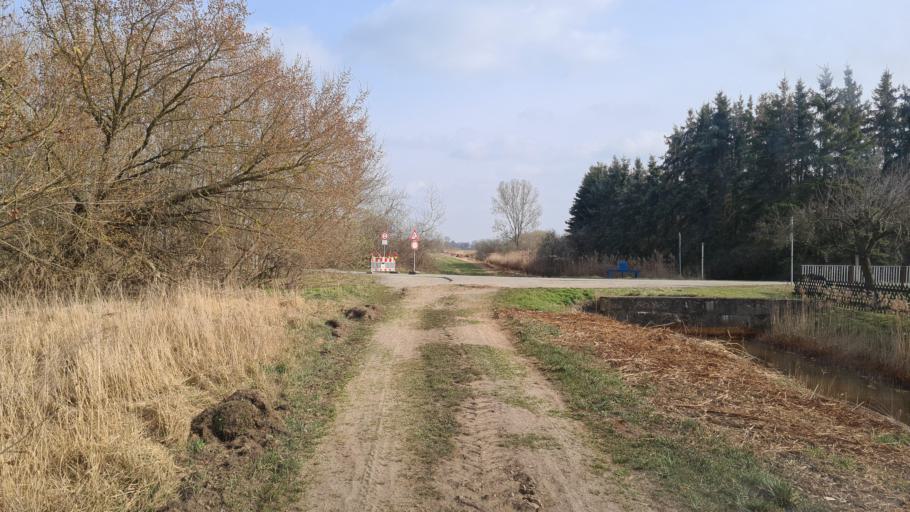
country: DE
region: Brandenburg
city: Plessa
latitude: 51.4351
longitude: 13.6330
